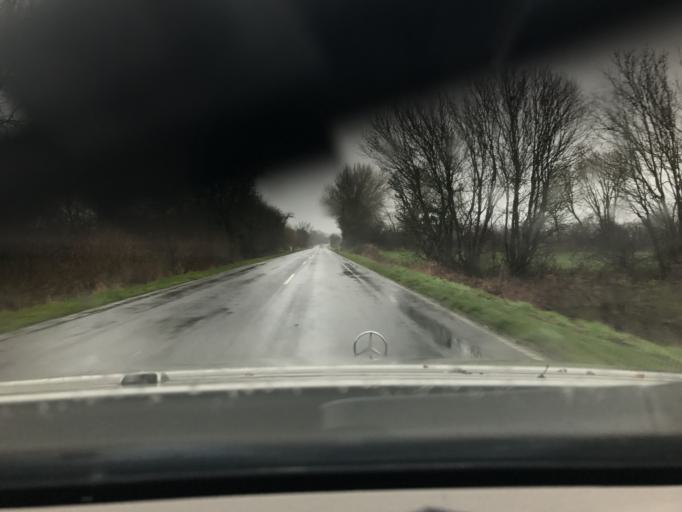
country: DK
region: South Denmark
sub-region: Sonderborg Kommune
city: Horuphav
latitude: 54.8744
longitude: 9.9953
